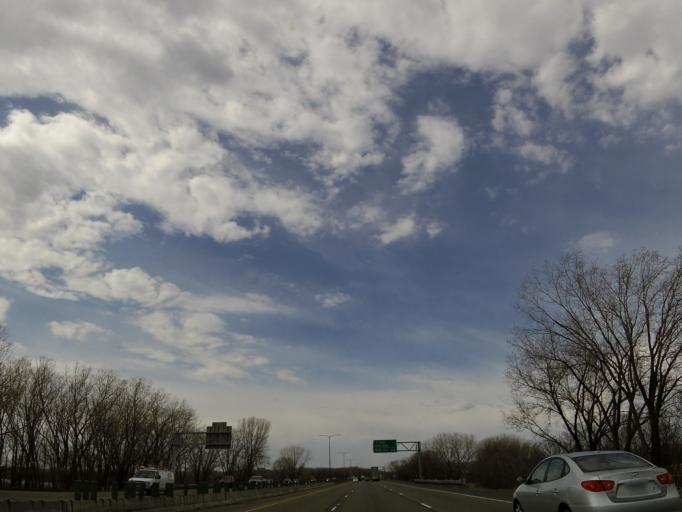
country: US
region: Minnesota
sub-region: Dakota County
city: Mendota Heights
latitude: 44.8614
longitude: -93.1850
